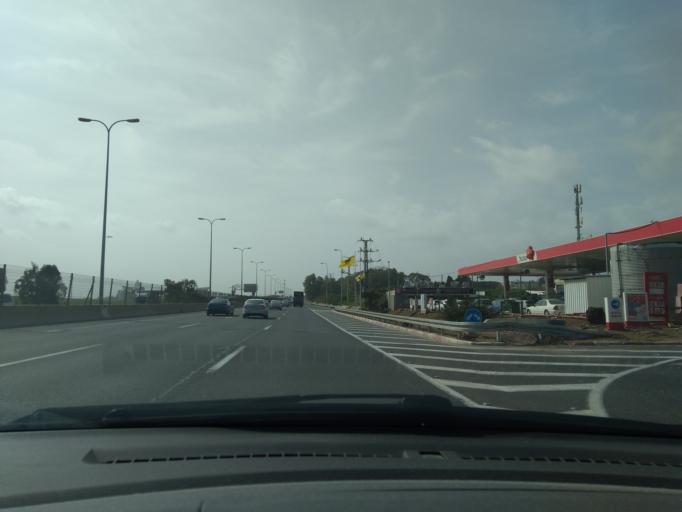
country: IL
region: Central District
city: Netanya
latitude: 32.3045
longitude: 34.8640
